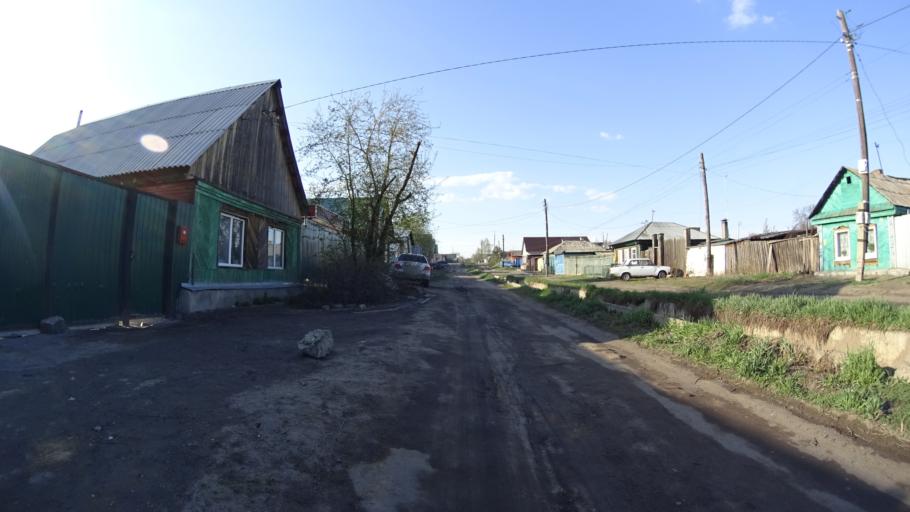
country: RU
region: Chelyabinsk
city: Troitsk
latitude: 54.0944
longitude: 61.5900
